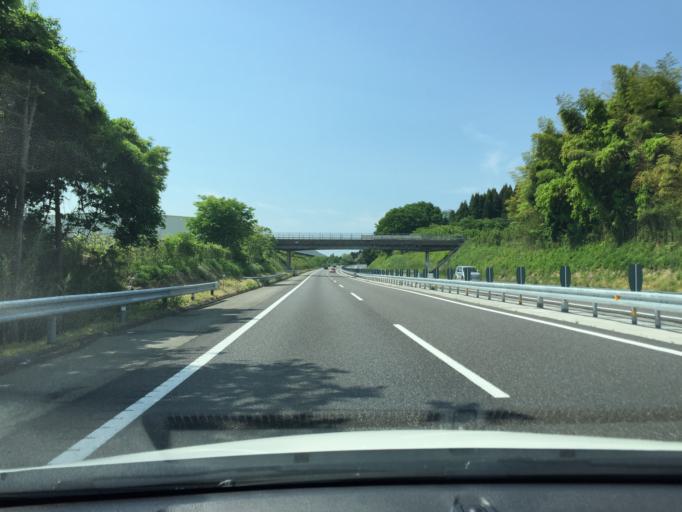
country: JP
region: Fukushima
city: Sukagawa
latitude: 37.2114
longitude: 140.3083
